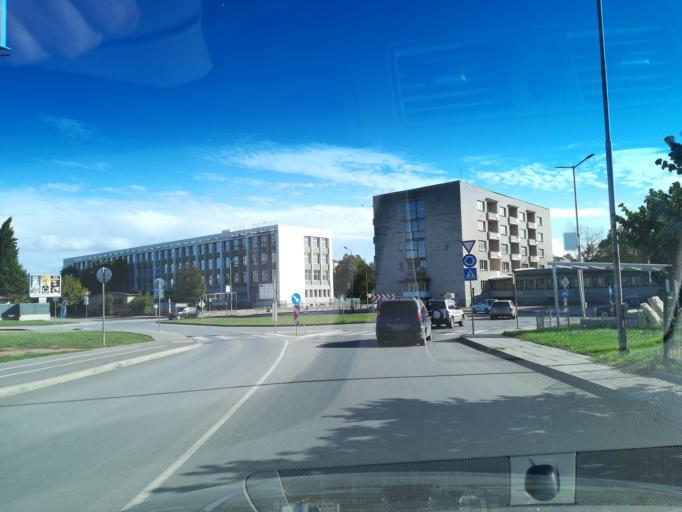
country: BG
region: Stara Zagora
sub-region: Obshtina Stara Zagora
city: Stara Zagora
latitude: 42.4318
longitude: 25.6387
